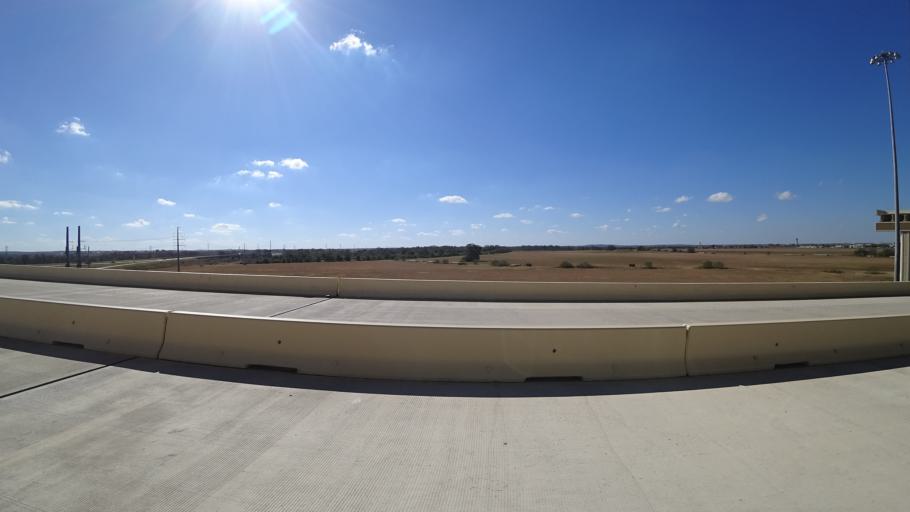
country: US
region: Texas
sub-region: Travis County
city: Hornsby Bend
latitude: 30.1960
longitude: -97.6264
